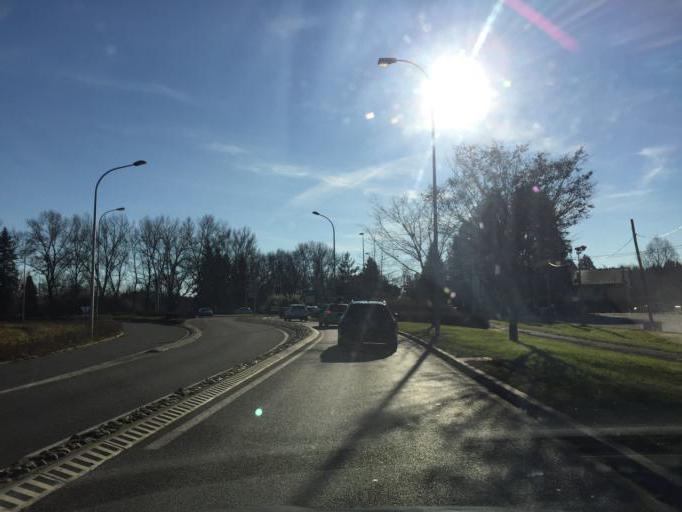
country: FR
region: Auvergne
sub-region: Departement de l'Allier
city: Bellerive-sur-Allier
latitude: 46.1418
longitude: 3.3971
